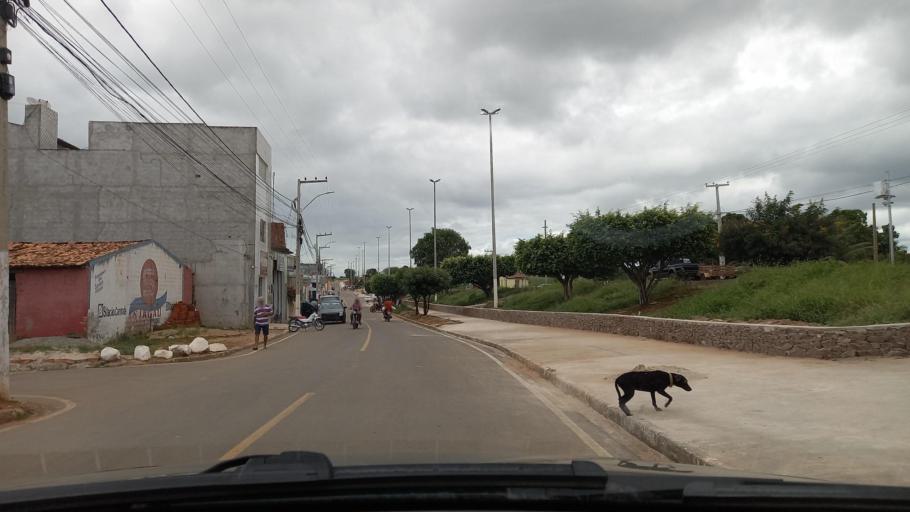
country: BR
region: Sergipe
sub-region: Caninde De Sao Francisco
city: Caninde de Sao Francisco
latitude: -9.6743
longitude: -37.7931
